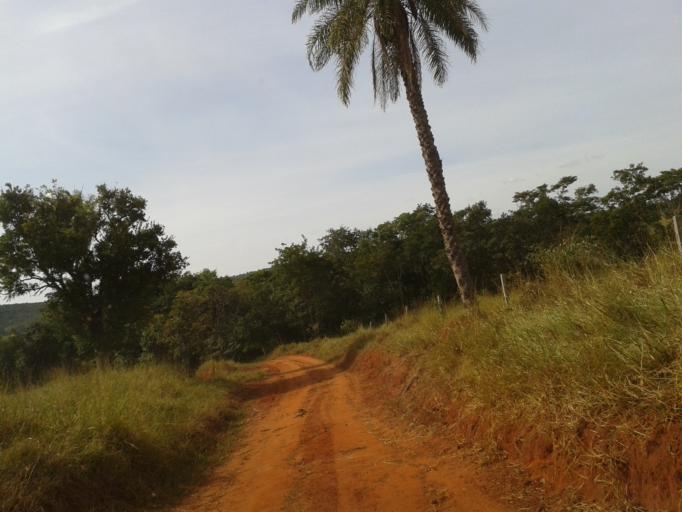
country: BR
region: Minas Gerais
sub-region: Campina Verde
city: Campina Verde
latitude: -19.5043
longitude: -49.5870
